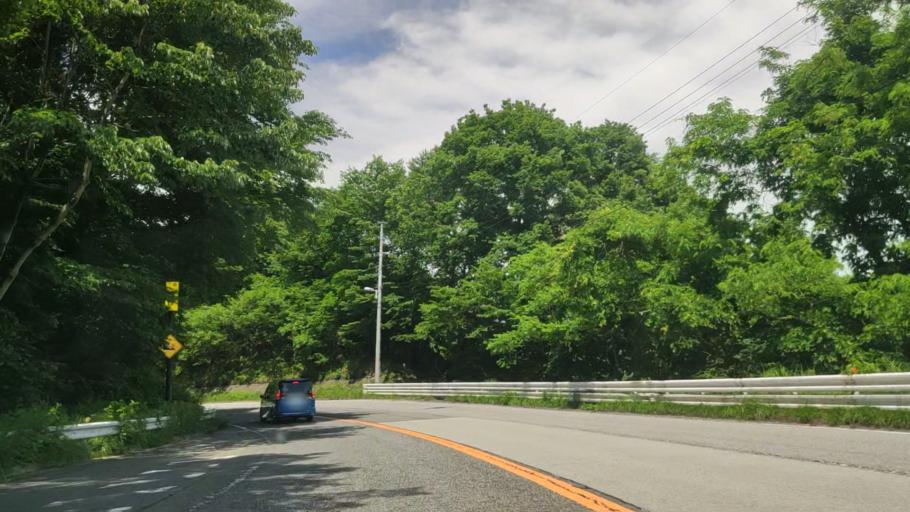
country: JP
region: Nagano
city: Saku
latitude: 36.3204
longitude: 138.6620
